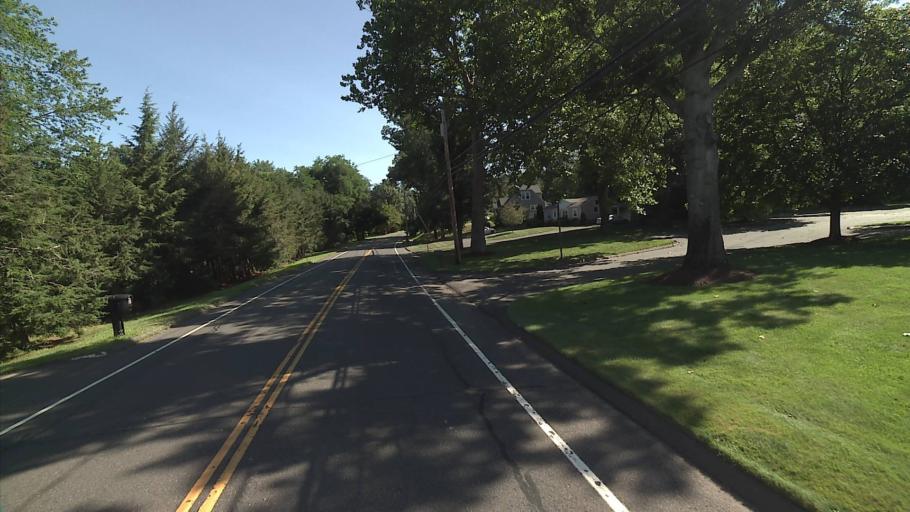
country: US
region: Connecticut
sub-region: Hartford County
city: Plainville
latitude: 41.6941
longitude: -72.8483
